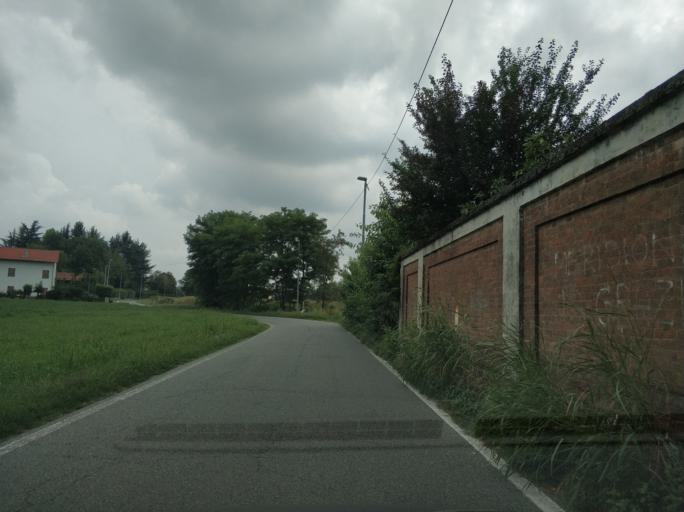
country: IT
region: Piedmont
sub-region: Provincia di Torino
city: Caselle Torinese
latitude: 45.1779
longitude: 7.6279
